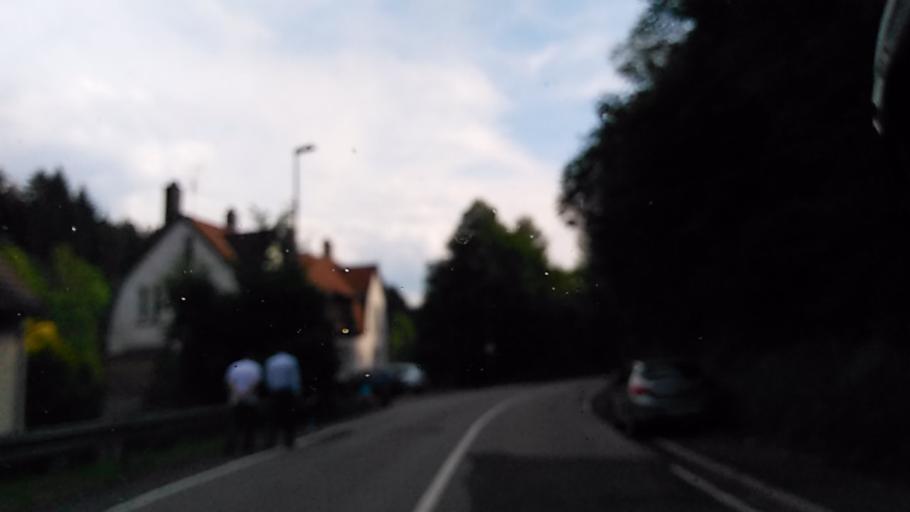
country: DE
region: North Rhine-Westphalia
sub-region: Regierungsbezirk Arnsberg
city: Herscheid
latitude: 51.2314
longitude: 7.7017
